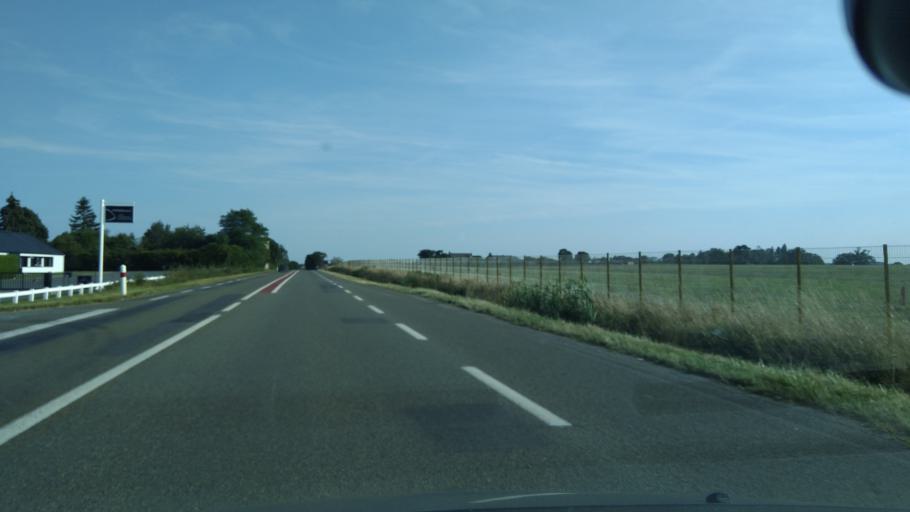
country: FR
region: Pays de la Loire
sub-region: Departement de la Mayenne
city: Entrammes
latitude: 48.0291
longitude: -0.7365
